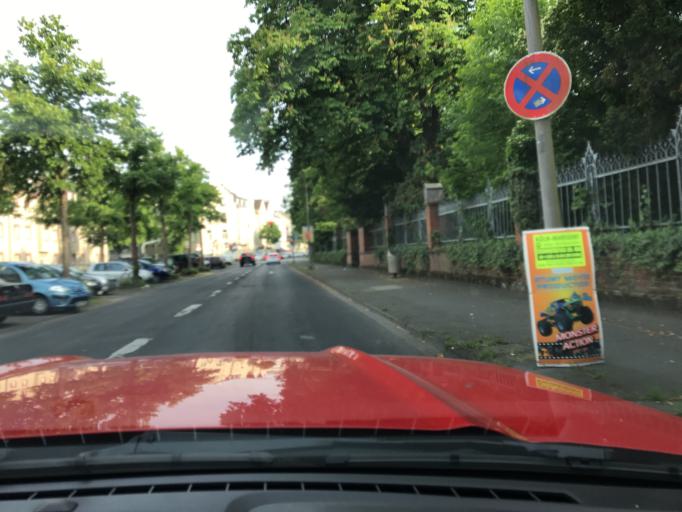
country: DE
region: North Rhine-Westphalia
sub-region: Regierungsbezirk Koln
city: Nippes
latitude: 50.9768
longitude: 6.9461
